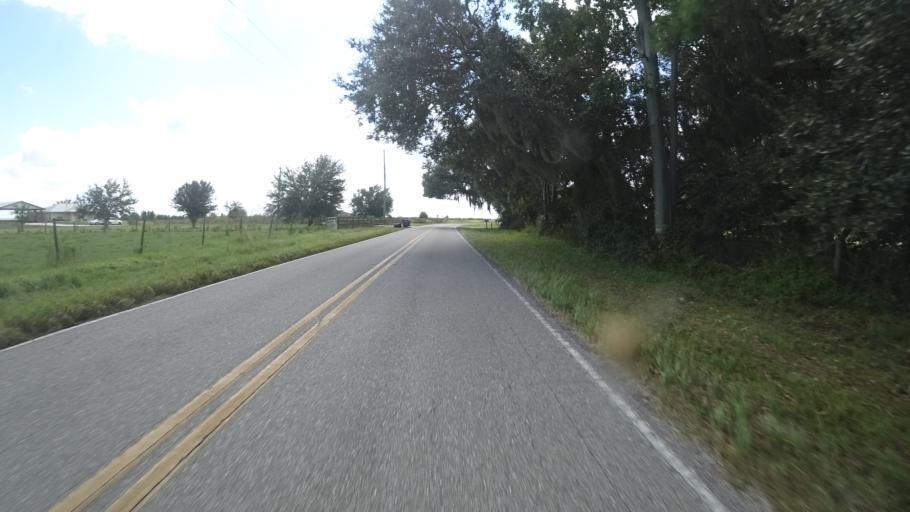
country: US
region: Florida
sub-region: Sarasota County
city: Lake Sarasota
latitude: 27.4004
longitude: -82.1307
